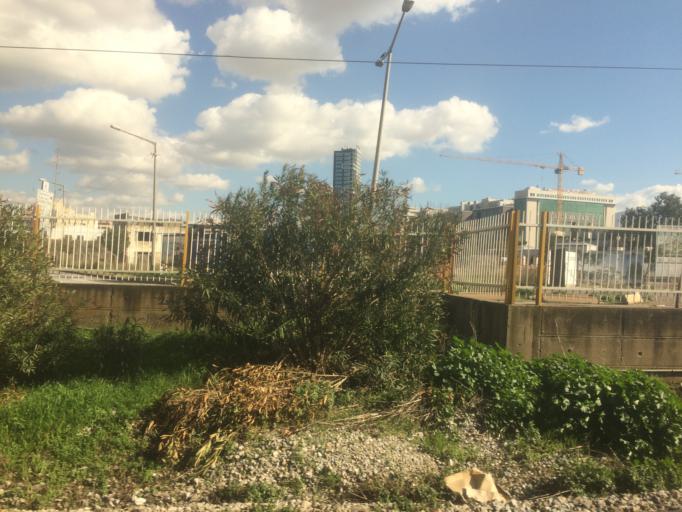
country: TR
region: Izmir
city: Buca
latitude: 38.4447
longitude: 27.1735
